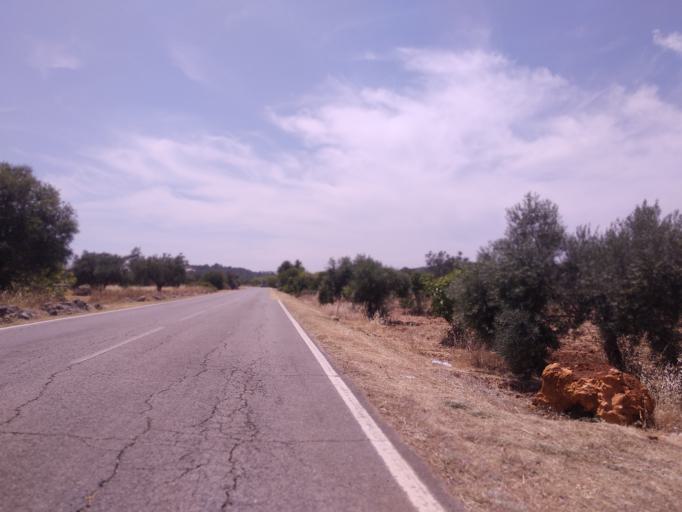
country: PT
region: Faro
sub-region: Sao Bras de Alportel
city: Sao Bras de Alportel
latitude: 37.1635
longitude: -7.9260
